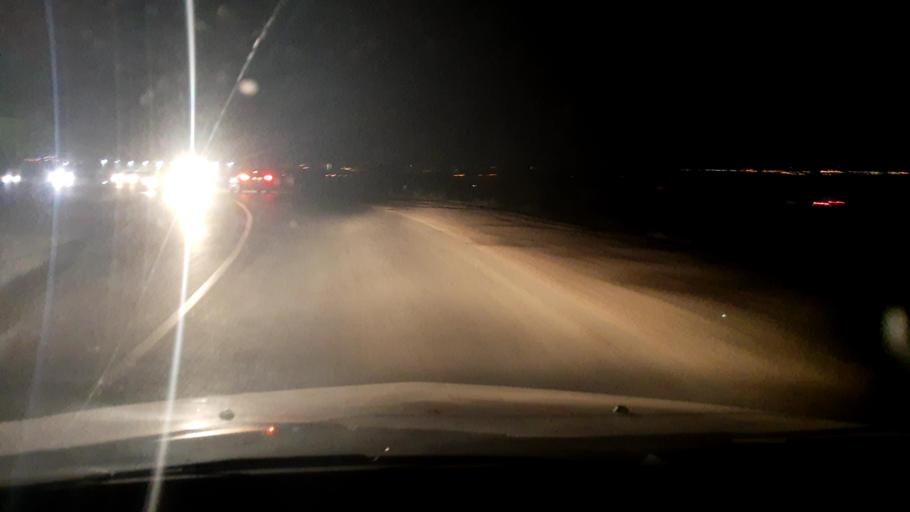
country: RU
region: Bashkortostan
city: Iglino
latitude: 54.7959
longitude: 56.2499
